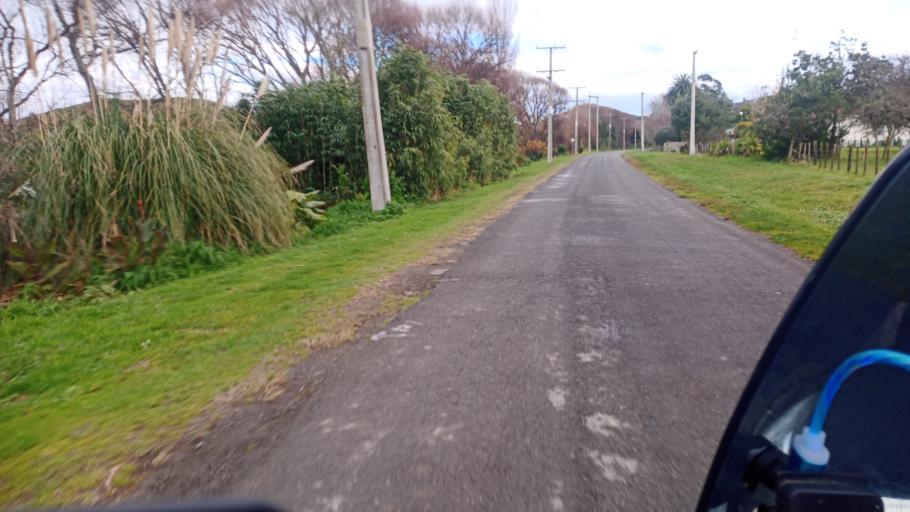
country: NZ
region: Gisborne
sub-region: Gisborne District
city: Gisborne
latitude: -38.3740
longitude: 178.2936
